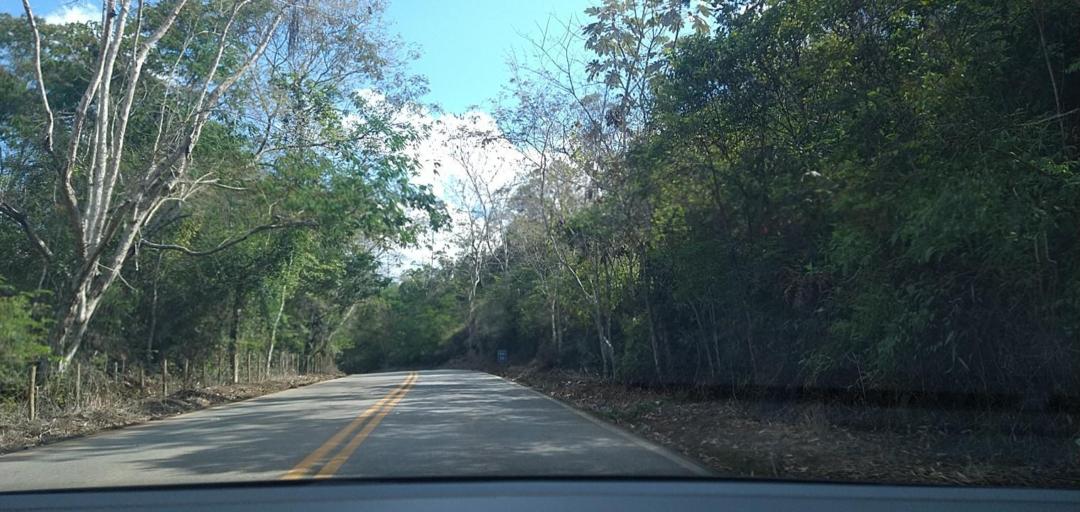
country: BR
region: Minas Gerais
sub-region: Alvinopolis
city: Alvinopolis
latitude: -20.0127
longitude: -43.0961
